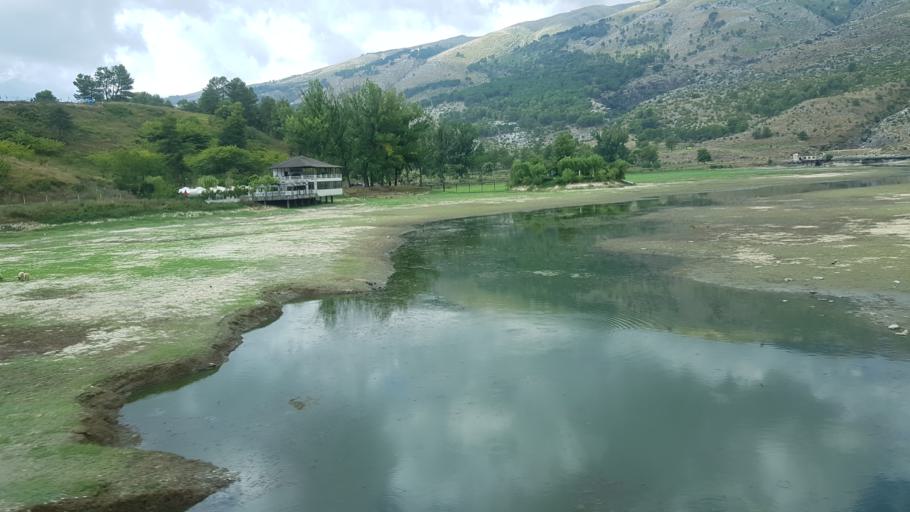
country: AL
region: Gjirokaster
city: Gjirokaster
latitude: 40.1020
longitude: 20.1261
